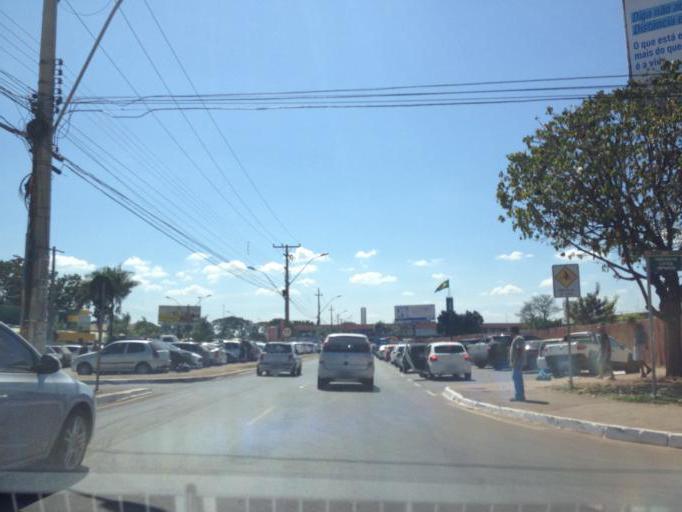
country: BR
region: Federal District
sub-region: Brasilia
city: Brasilia
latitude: -15.7977
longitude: -47.9493
